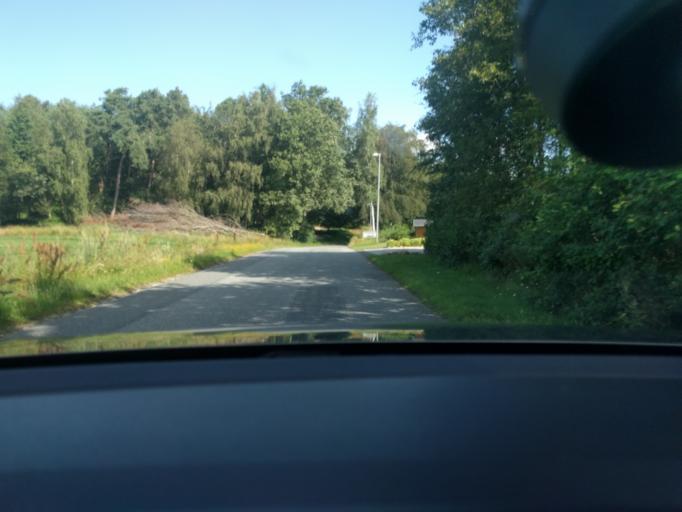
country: DK
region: Central Jutland
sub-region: Viborg Kommune
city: Viborg
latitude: 56.5086
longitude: 9.3049
